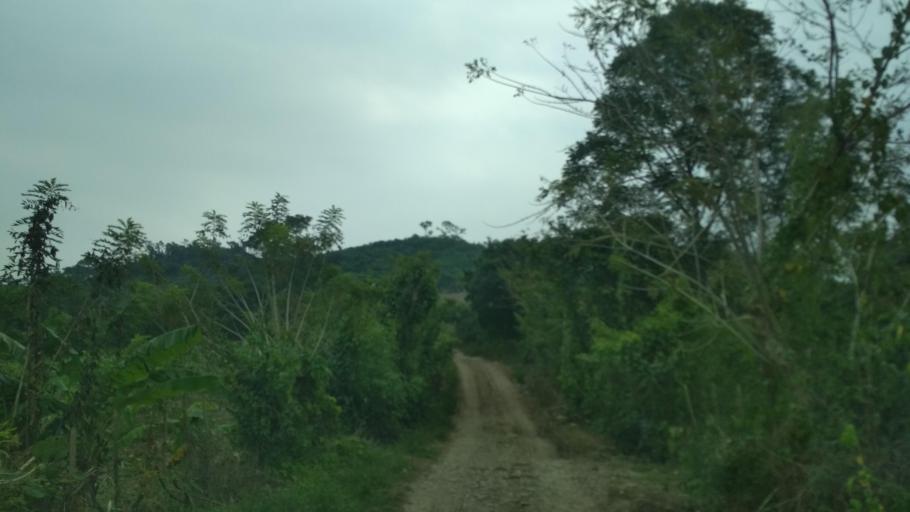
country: MM
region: Kayah
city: Loikaw
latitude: 20.2108
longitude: 97.3290
